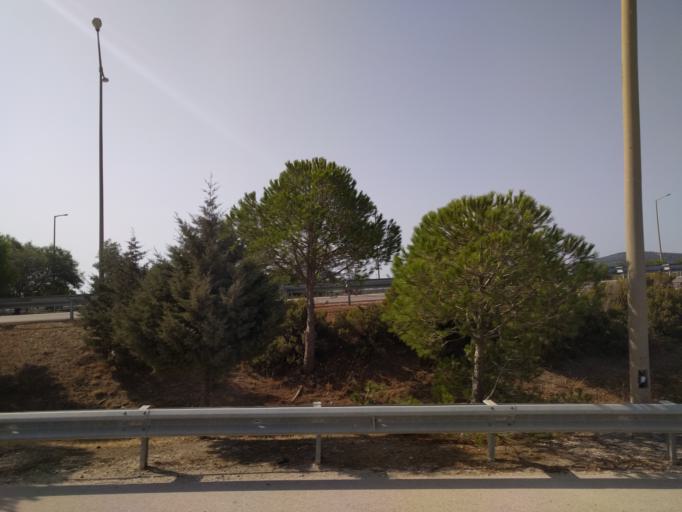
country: TR
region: Izmir
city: Alacati
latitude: 38.2783
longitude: 26.3840
